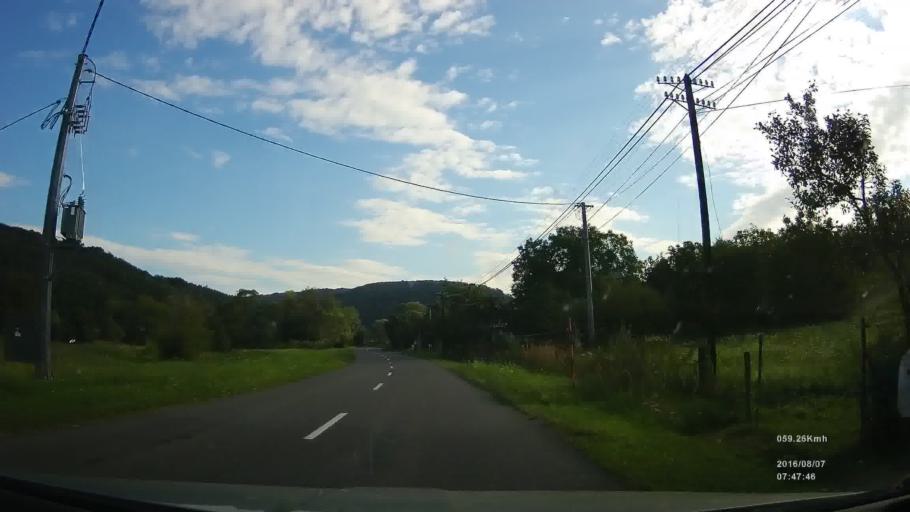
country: SK
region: Presovsky
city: Stropkov
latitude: 49.2812
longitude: 21.7560
